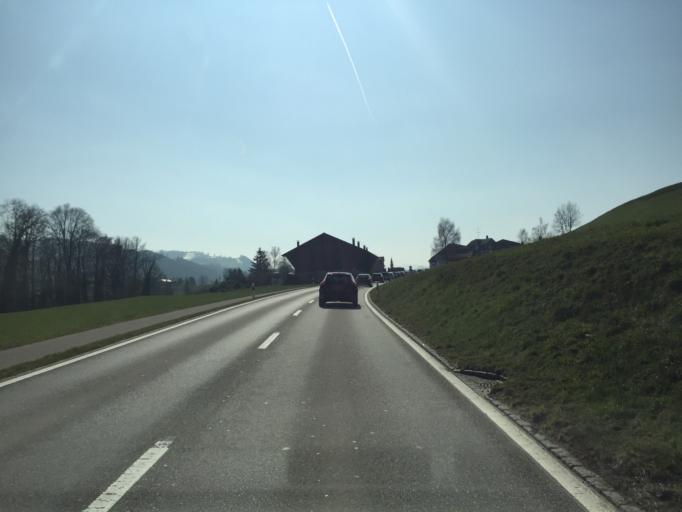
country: CH
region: Saint Gallen
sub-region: Wahlkreis Toggenburg
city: Lutisburg
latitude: 47.3897
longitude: 9.0761
